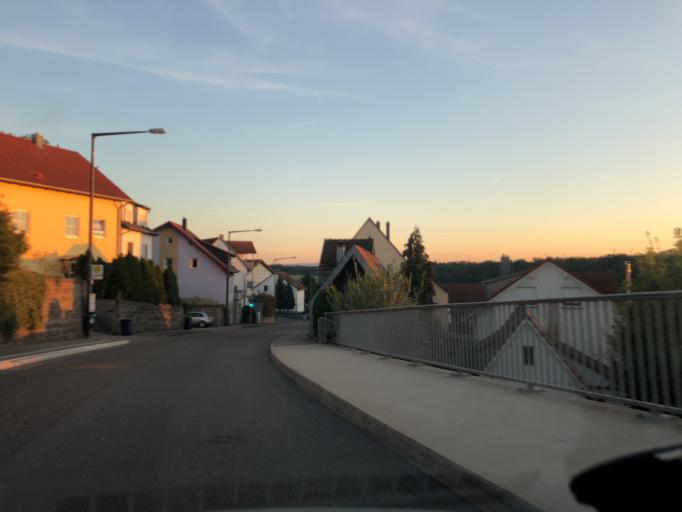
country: DE
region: Baden-Wuerttemberg
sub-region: Regierungsbezirk Stuttgart
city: Marbach am Neckar
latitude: 48.9056
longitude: 9.2650
